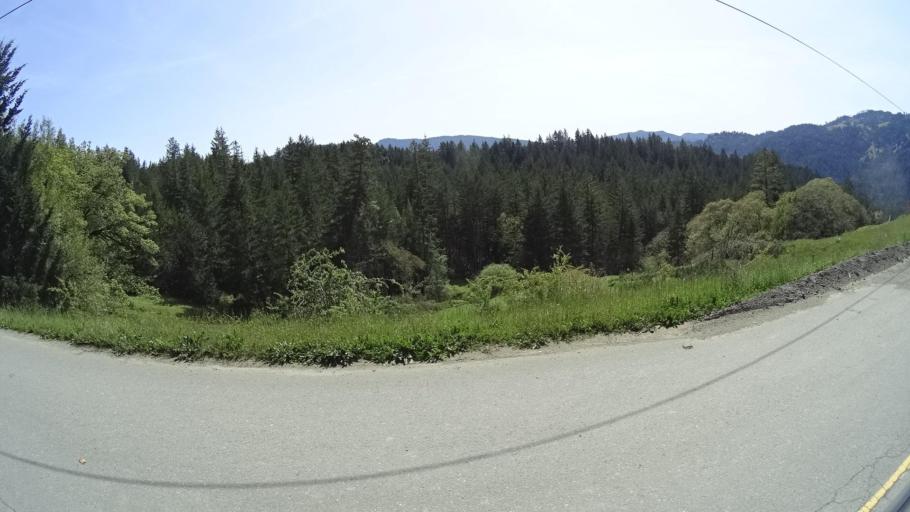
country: US
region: California
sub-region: Humboldt County
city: Redway
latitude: 40.4191
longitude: -123.7626
